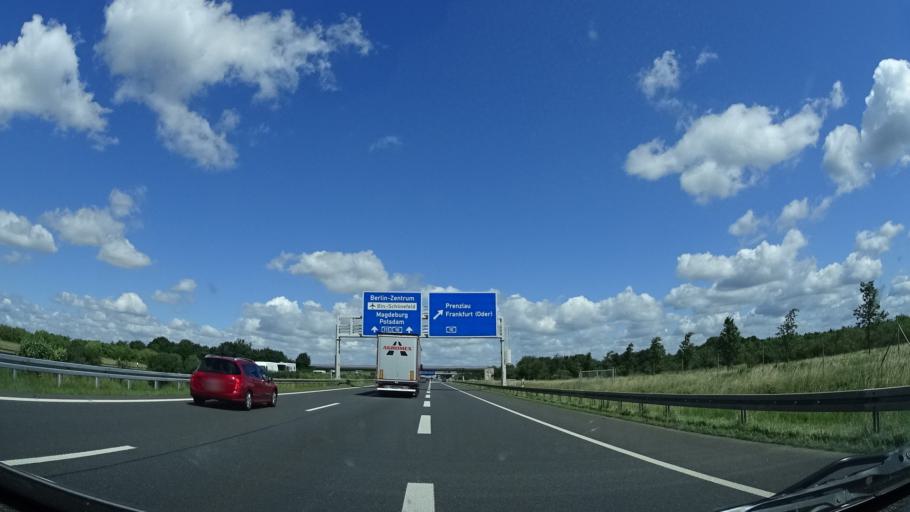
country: DE
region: Brandenburg
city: Mittenwalde
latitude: 52.3108
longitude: 13.5555
